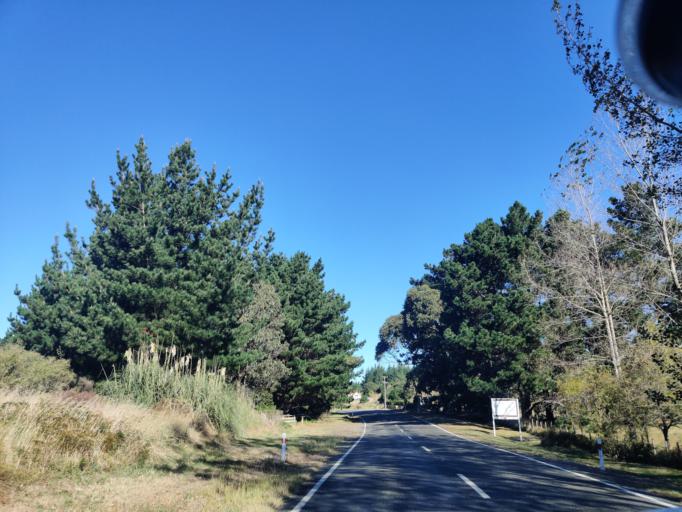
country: NZ
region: Manawatu-Wanganui
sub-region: Horowhenua District
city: Foxton
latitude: -40.3728
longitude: 175.2476
